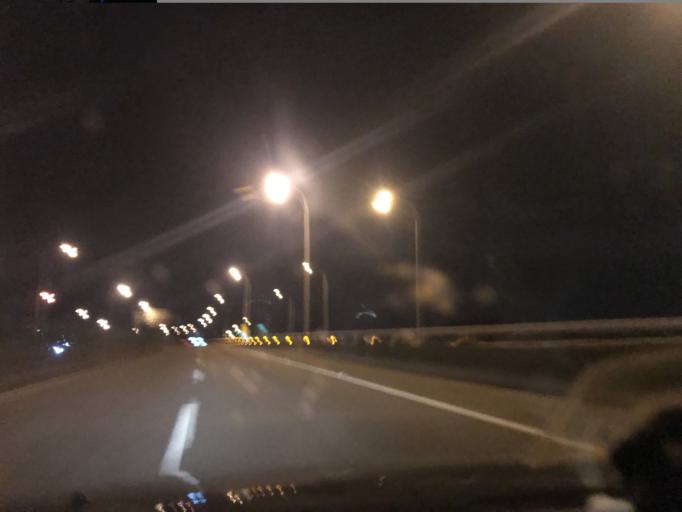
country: TW
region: Taiwan
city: Daxi
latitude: 24.9262
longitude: 121.2177
